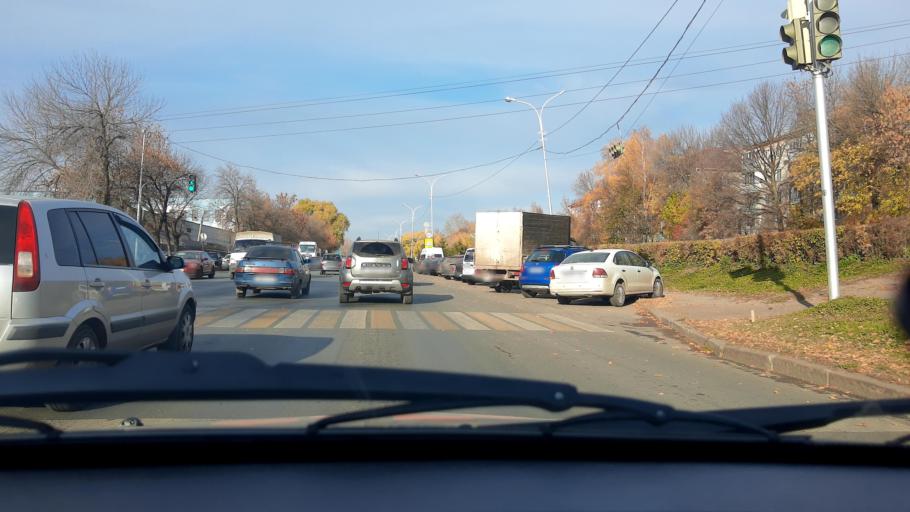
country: RU
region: Bashkortostan
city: Ufa
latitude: 54.8052
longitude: 56.1067
